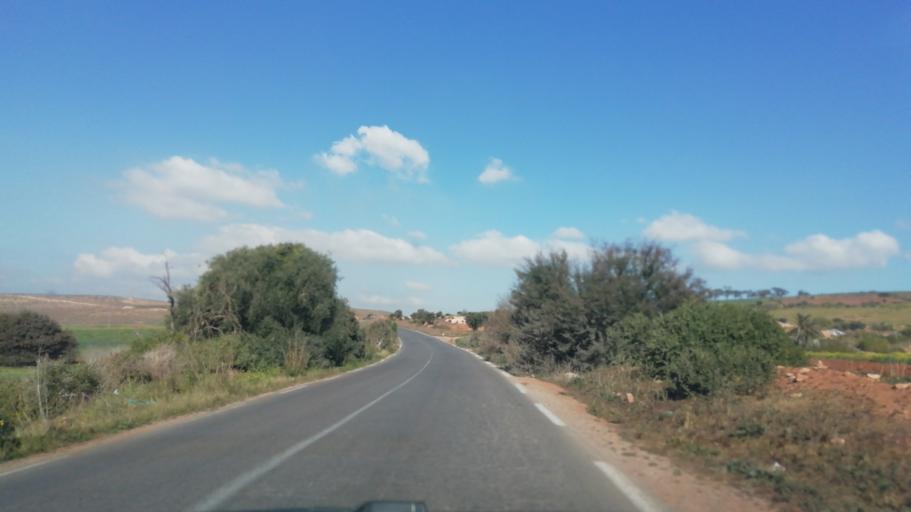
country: DZ
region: Oran
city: Ain el Bya
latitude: 35.7376
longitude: -0.2538
